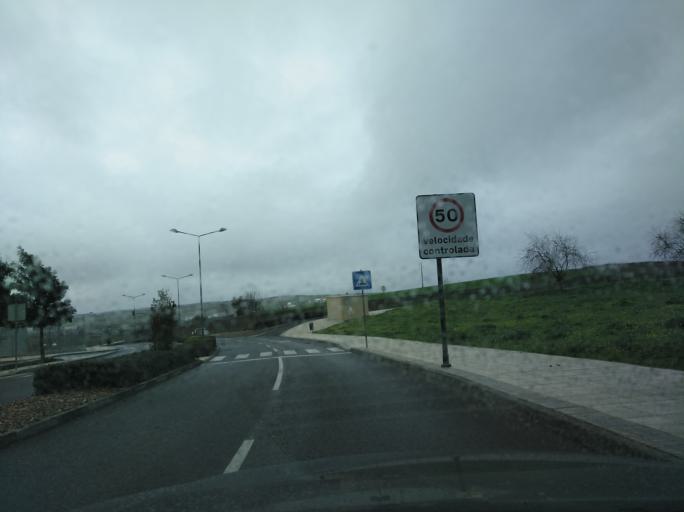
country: PT
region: Portalegre
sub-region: Campo Maior
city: Campo Maior
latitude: 39.0204
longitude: -7.0687
